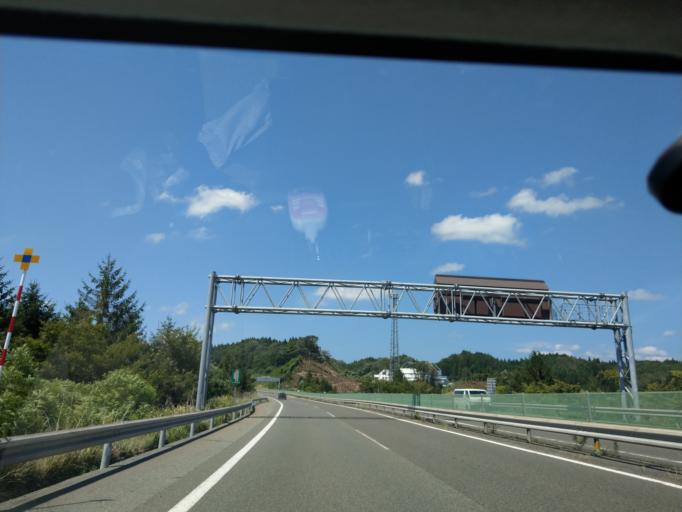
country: JP
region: Akita
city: Akita
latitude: 39.6505
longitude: 140.2060
